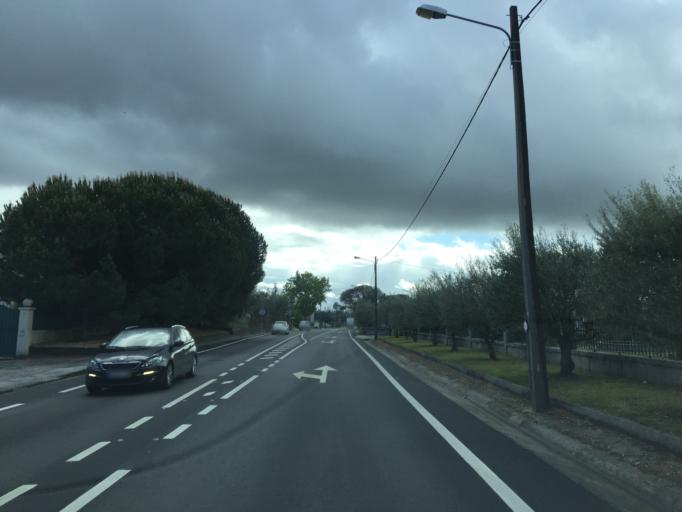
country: PT
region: Coimbra
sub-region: Oliveira do Hospital
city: Oliveira do Hospital
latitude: 40.3212
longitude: -7.8834
